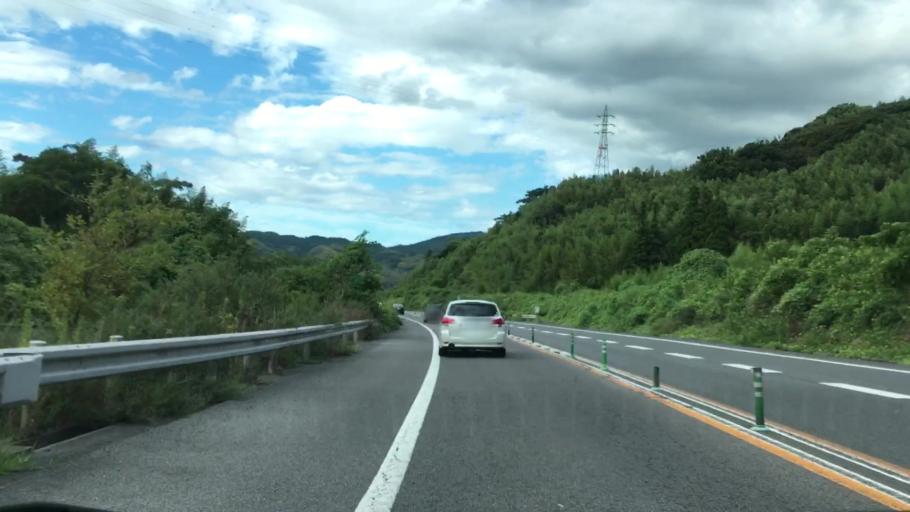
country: JP
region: Saga Prefecture
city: Karatsu
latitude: 33.4322
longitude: 130.0484
